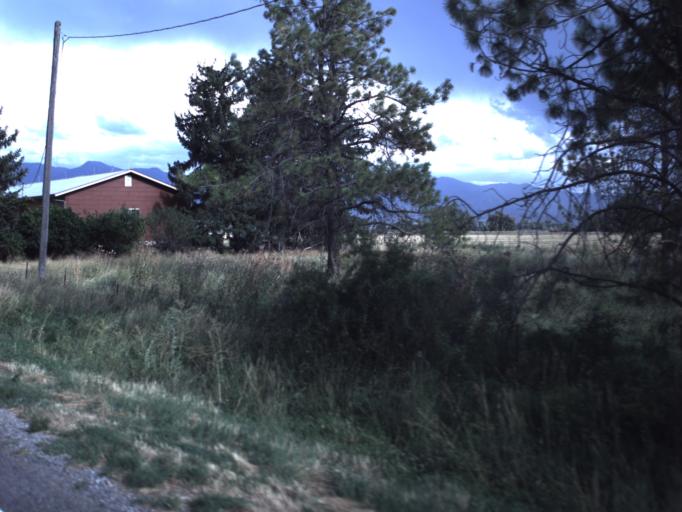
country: US
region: Utah
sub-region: Cache County
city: Lewiston
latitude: 41.9754
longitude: -111.9299
